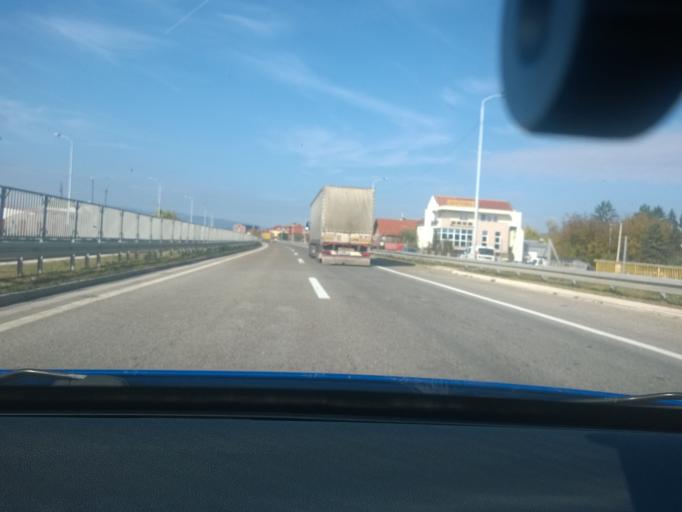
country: RS
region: Central Serbia
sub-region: Nisavski Okrug
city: Nis
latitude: 43.3449
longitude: 21.8798
